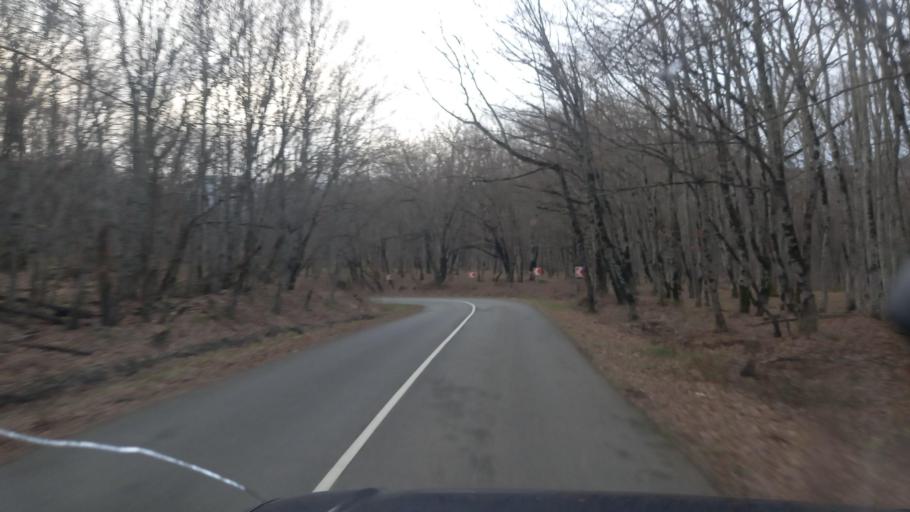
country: RU
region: Krasnodarskiy
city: Goryachiy Klyuch
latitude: 44.3875
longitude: 39.1814
